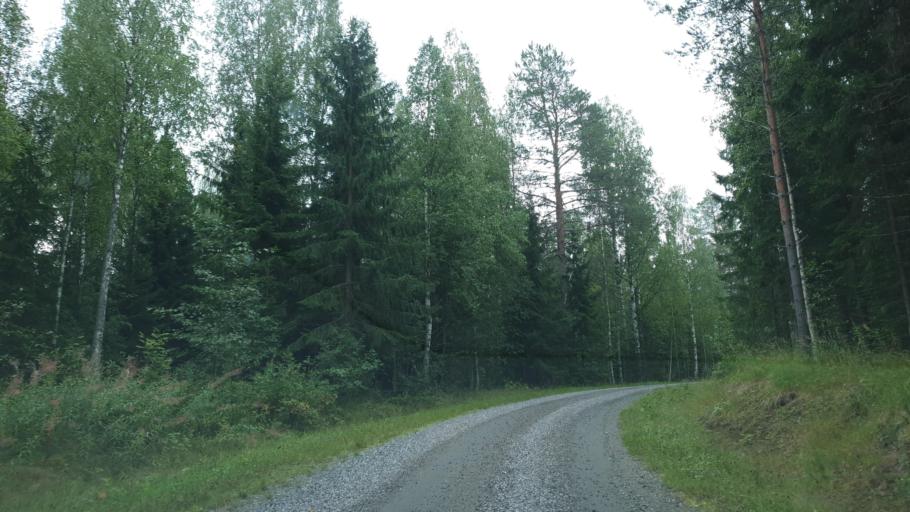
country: FI
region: Northern Savo
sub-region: Kuopio
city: Nilsiae
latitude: 63.2476
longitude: 28.2575
